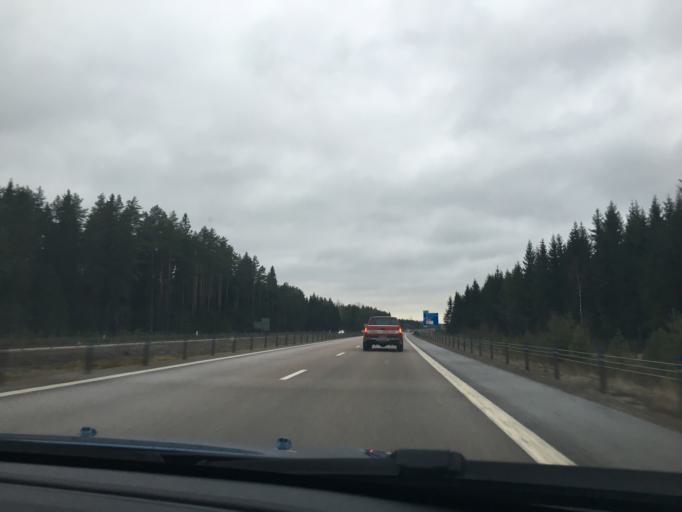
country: SE
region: Uppsala
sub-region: Alvkarleby Kommun
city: AElvkarleby
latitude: 60.4472
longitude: 17.4169
